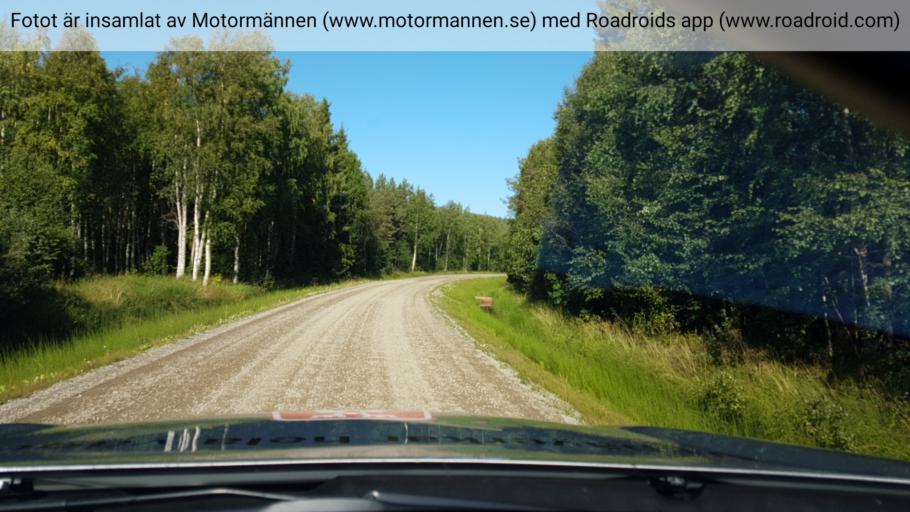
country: SE
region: Norrbotten
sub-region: Kalix Kommun
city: Kalix
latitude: 66.1840
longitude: 23.1999
